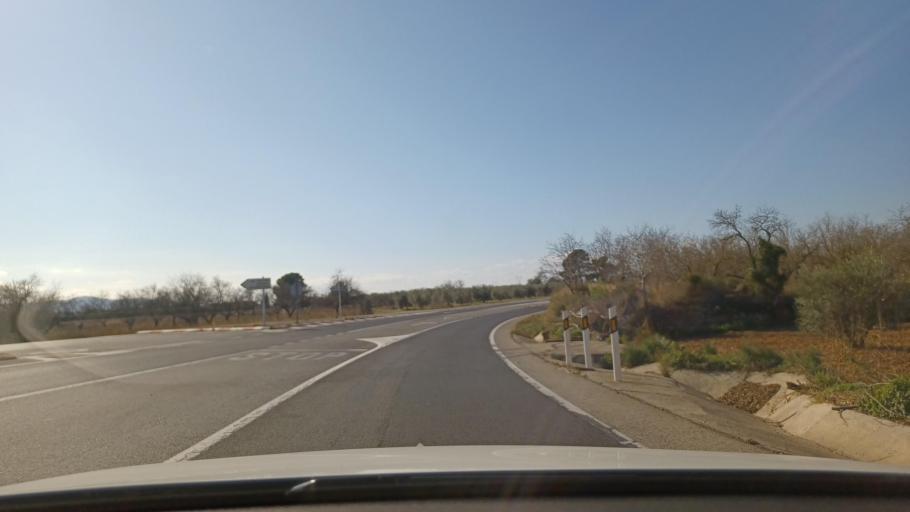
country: ES
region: Catalonia
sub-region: Provincia de Tarragona
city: Santa Barbara
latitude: 40.6784
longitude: 0.4584
